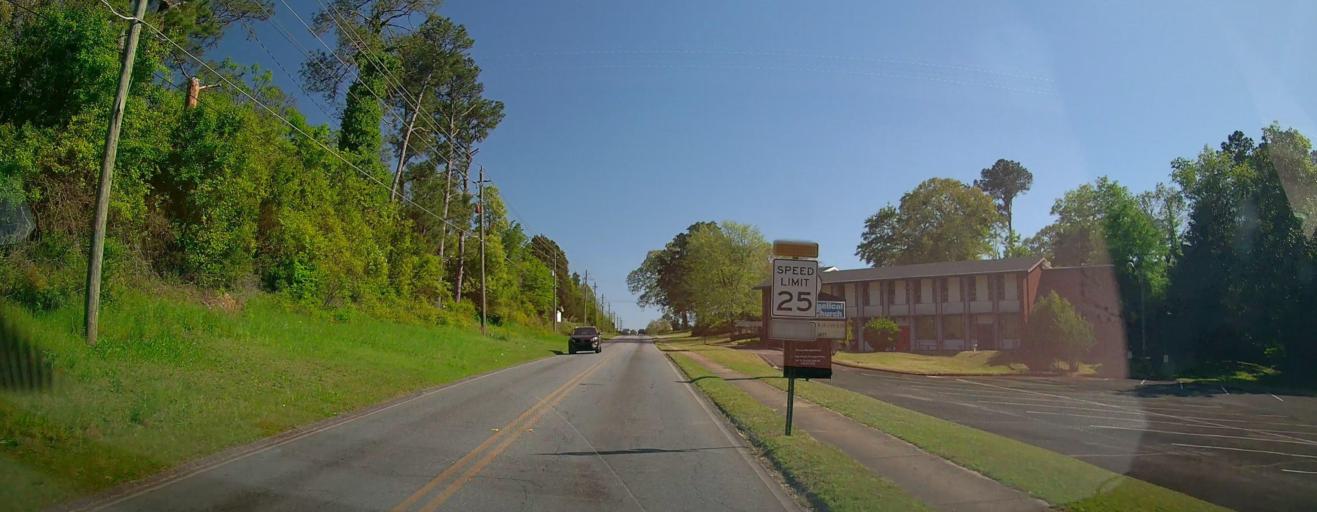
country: US
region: Georgia
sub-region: Houston County
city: Warner Robins
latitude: 32.6241
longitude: -83.6225
